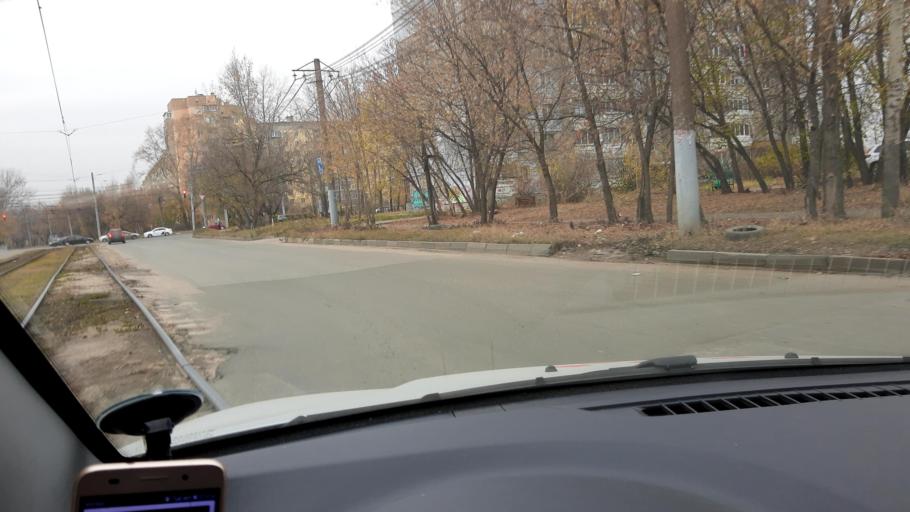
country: RU
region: Nizjnij Novgorod
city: Nizhniy Novgorod
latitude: 56.3346
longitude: 43.9215
